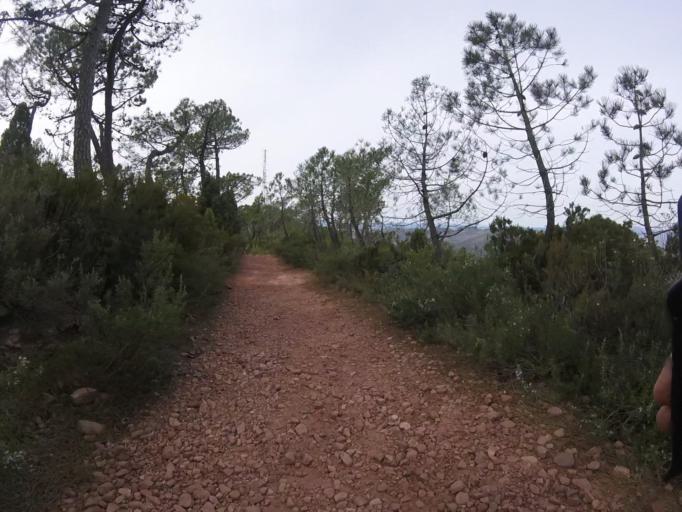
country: ES
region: Valencia
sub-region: Provincia de Castello
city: Benicassim
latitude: 40.0847
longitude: 0.0272
